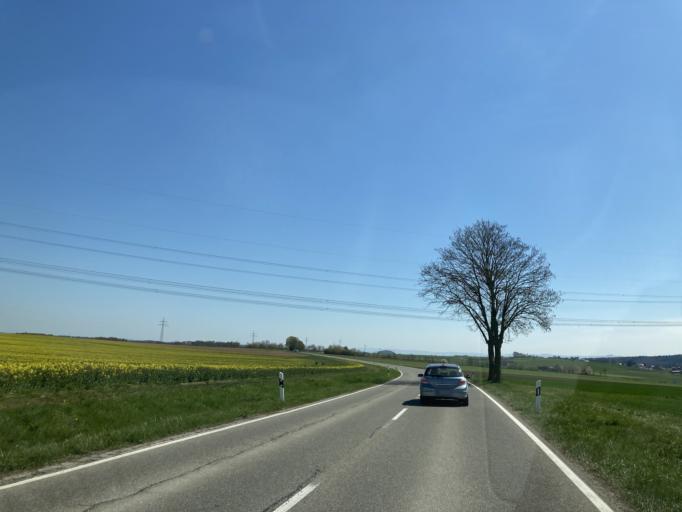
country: DE
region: Baden-Wuerttemberg
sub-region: Regierungsbezirk Stuttgart
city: Bondorf
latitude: 48.4968
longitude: 8.8261
